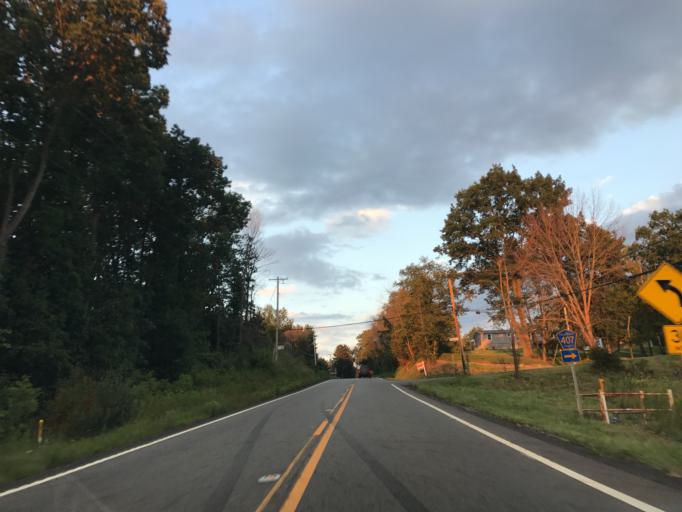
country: US
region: Ohio
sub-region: Columbiana County
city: Lisbon
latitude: 40.7557
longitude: -80.9030
